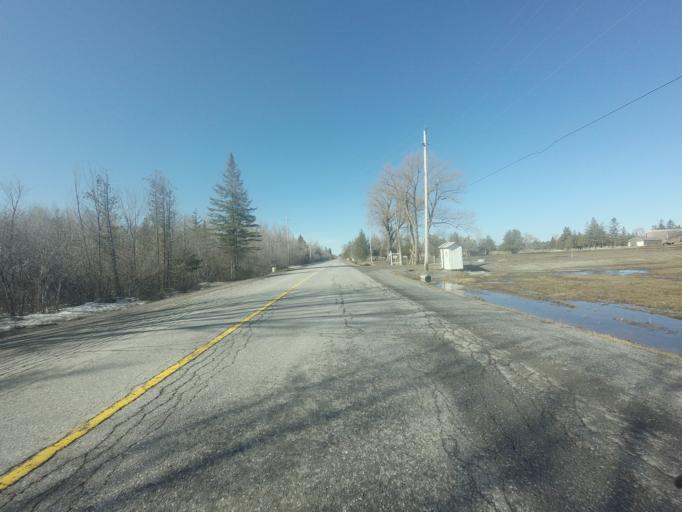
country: CA
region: Ontario
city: Carleton Place
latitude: 45.1976
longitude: -75.9935
